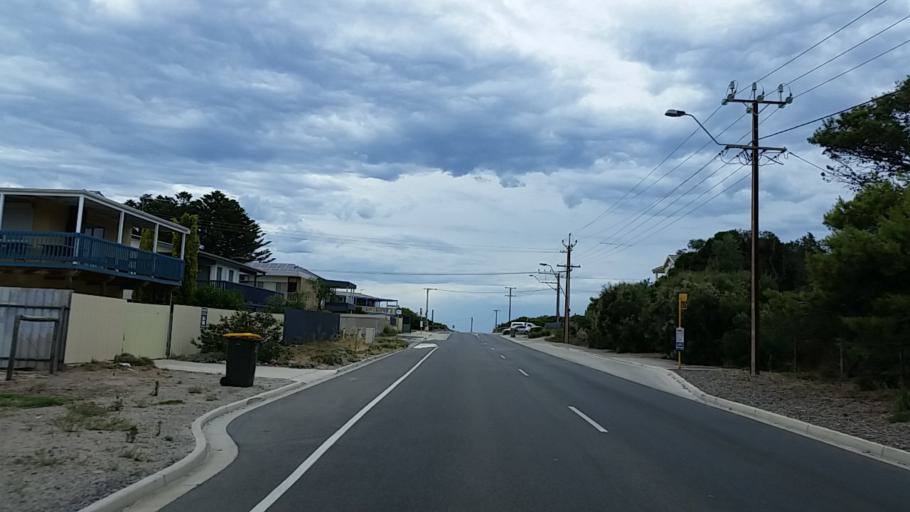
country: AU
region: South Australia
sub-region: Onkaparinga
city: Port Willunga
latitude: -35.3086
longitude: 138.4511
